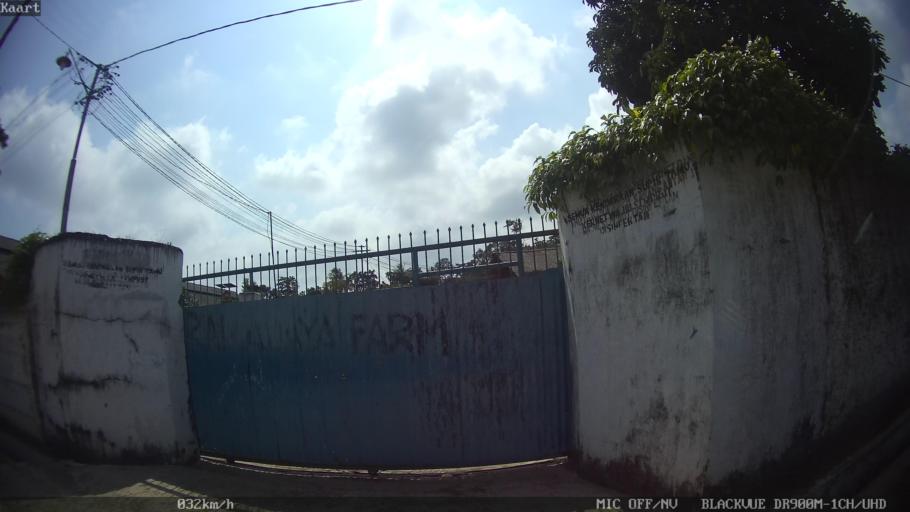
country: ID
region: Lampung
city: Kedaton
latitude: -5.3344
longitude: 105.2729
